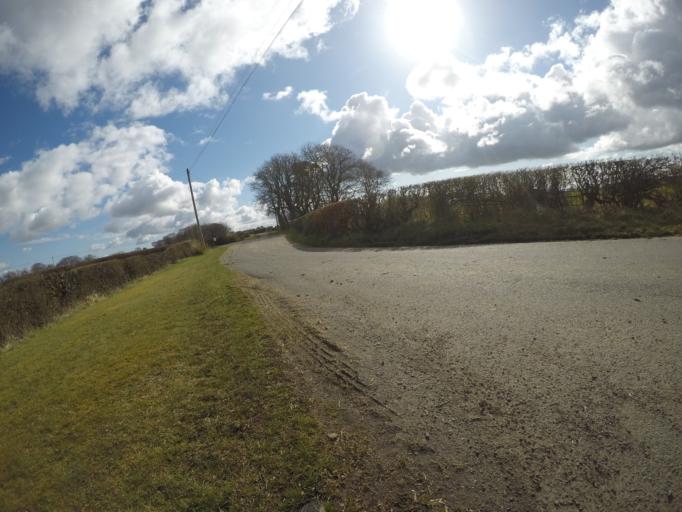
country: GB
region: Scotland
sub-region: North Ayrshire
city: Beith
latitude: 55.7124
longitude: -4.6521
